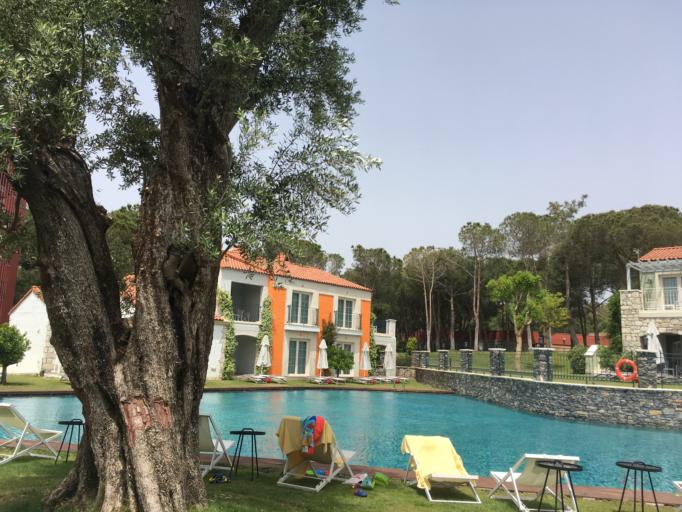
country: TR
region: Antalya
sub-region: Serik
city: Kumkoey
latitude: 36.8607
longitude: 30.9891
